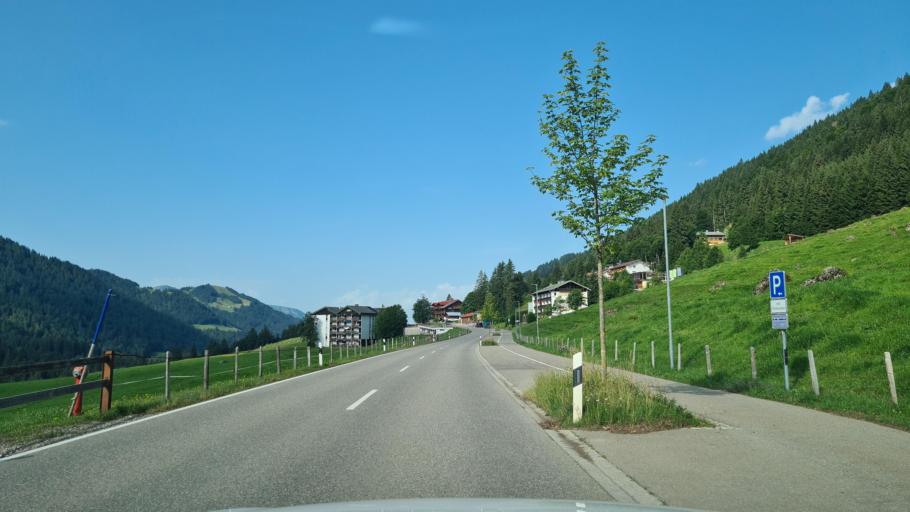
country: DE
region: Bavaria
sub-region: Swabia
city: Balderschwang
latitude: 47.4651
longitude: 10.0975
